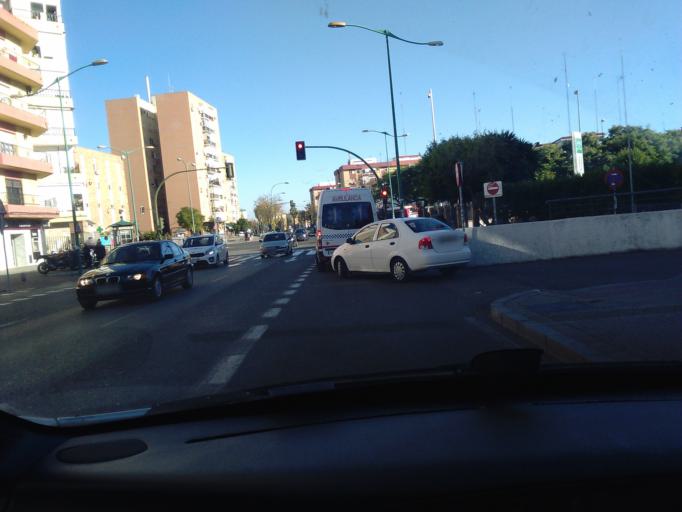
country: ES
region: Andalusia
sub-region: Provincia de Sevilla
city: Sevilla
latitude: 37.4075
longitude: -5.9862
